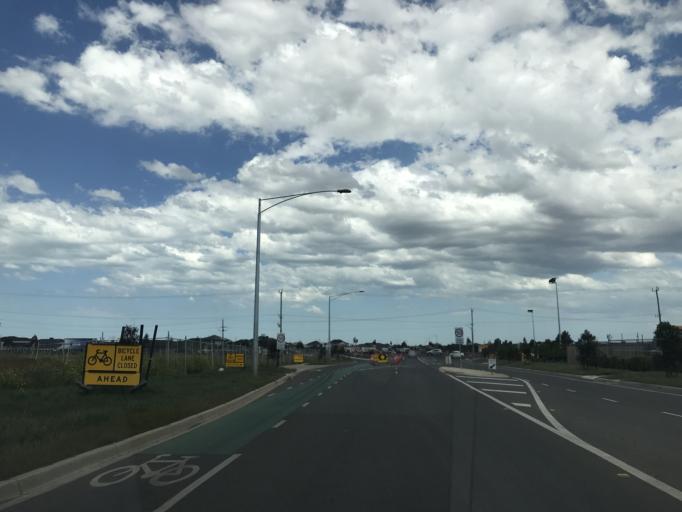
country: AU
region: Victoria
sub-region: Wyndham
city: Truganina
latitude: -37.8371
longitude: 144.7401
